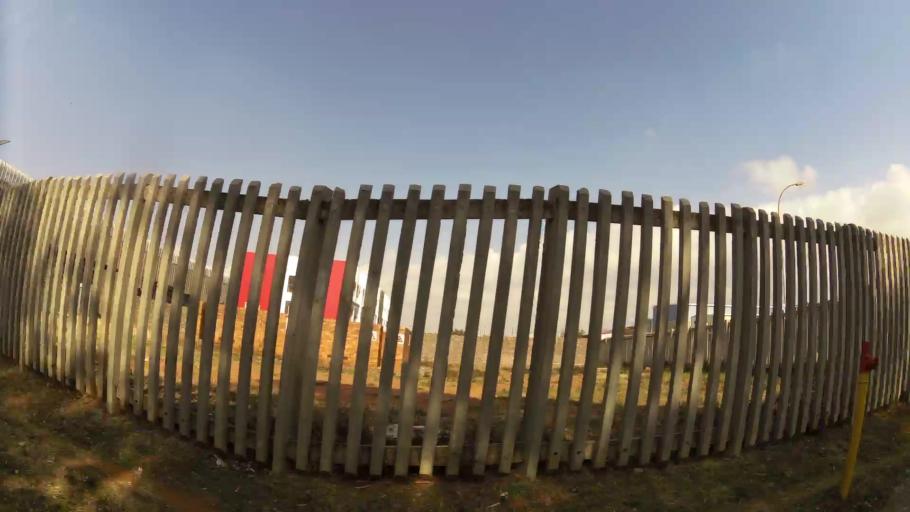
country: ZA
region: Gauteng
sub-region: Ekurhuleni Metropolitan Municipality
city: Germiston
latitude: -26.1643
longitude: 28.2007
